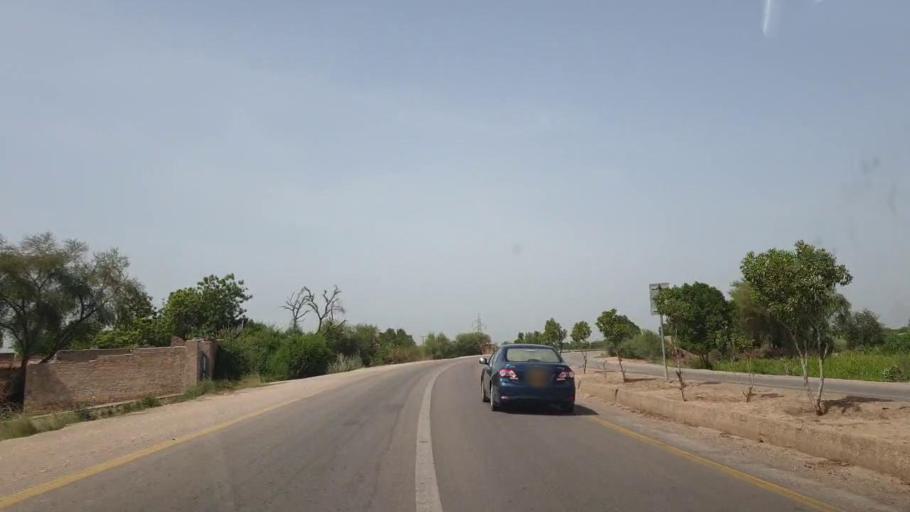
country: PK
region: Sindh
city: Sakrand
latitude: 26.1929
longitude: 68.2916
